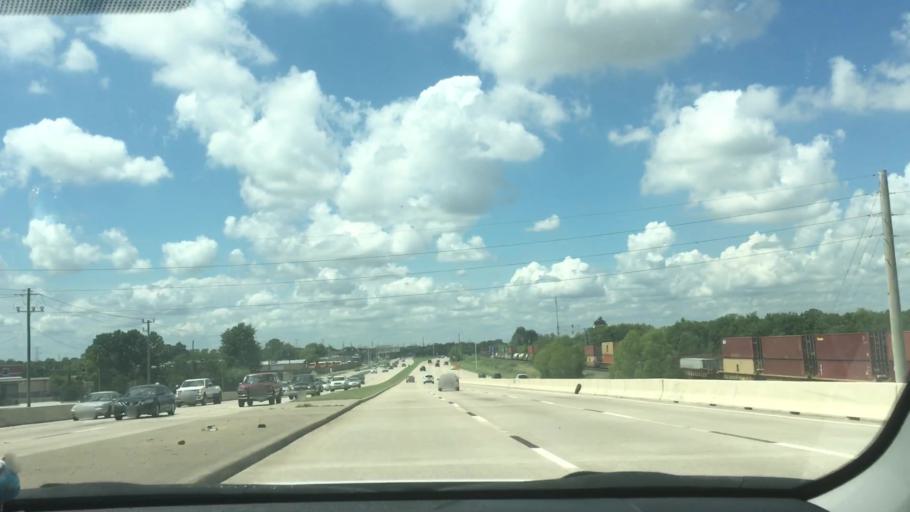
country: US
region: Texas
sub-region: Fort Bend County
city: Missouri City
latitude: 29.6182
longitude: -95.5396
